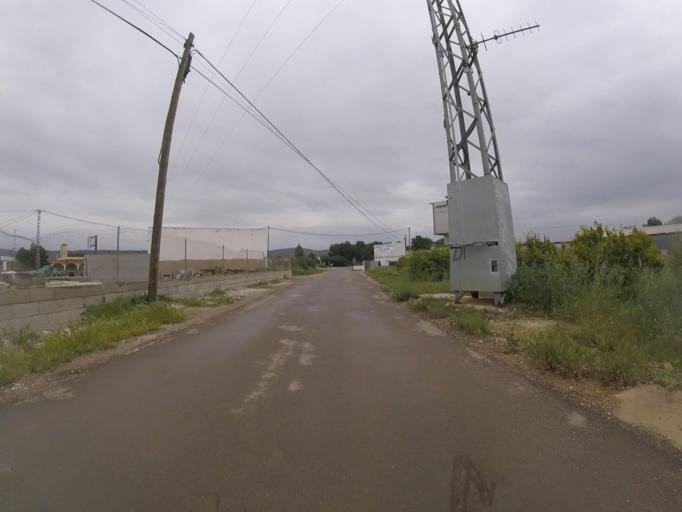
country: ES
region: Valencia
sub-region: Provincia de Castello
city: Alcala de Xivert
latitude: 40.2968
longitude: 0.2276
